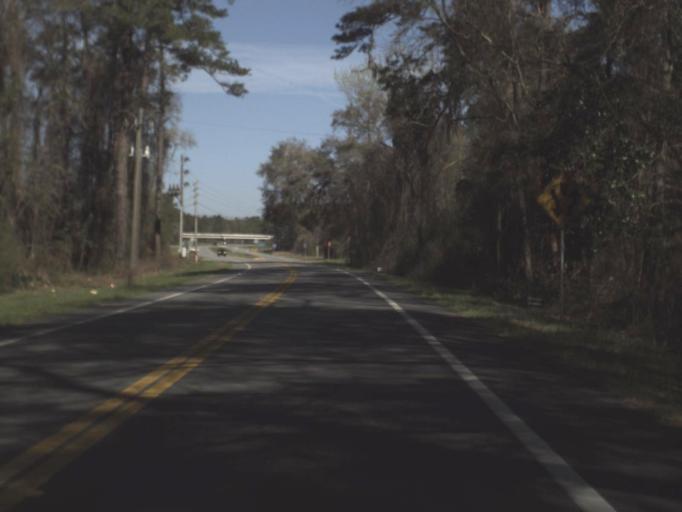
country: US
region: Florida
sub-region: Jefferson County
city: Monticello
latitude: 30.4821
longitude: -84.0229
